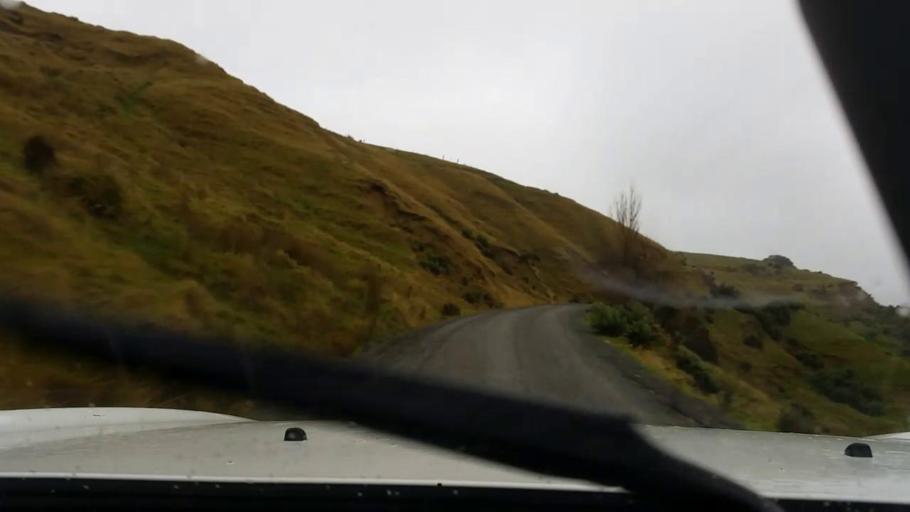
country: NZ
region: Wellington
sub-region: Masterton District
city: Masterton
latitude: -41.2499
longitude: 175.9080
